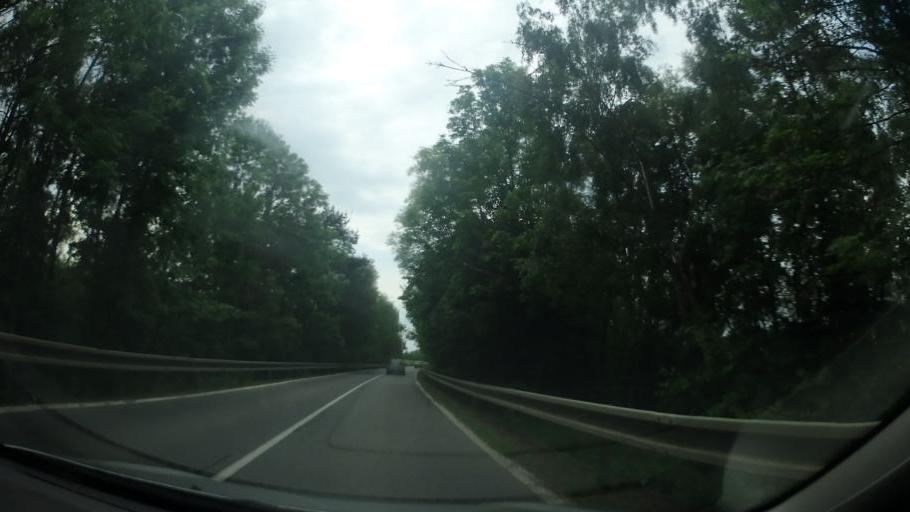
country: CZ
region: Vysocina
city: Bystrice nad Pernstejnem
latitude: 49.5180
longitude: 16.2944
